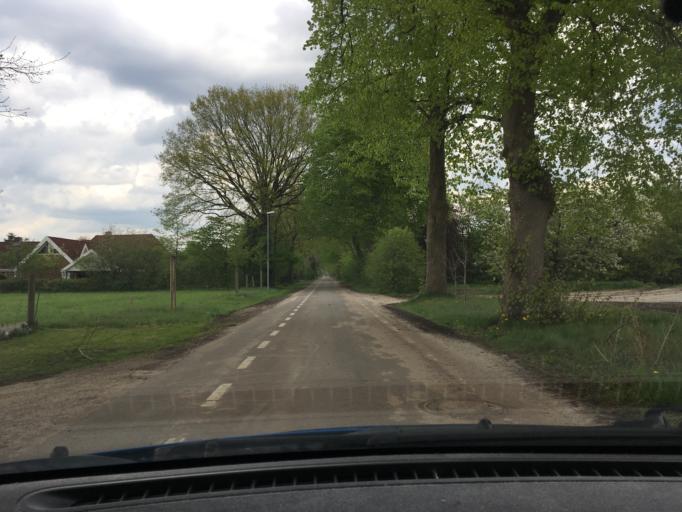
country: DE
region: Lower Saxony
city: Radbruch
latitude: 53.2995
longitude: 10.2698
